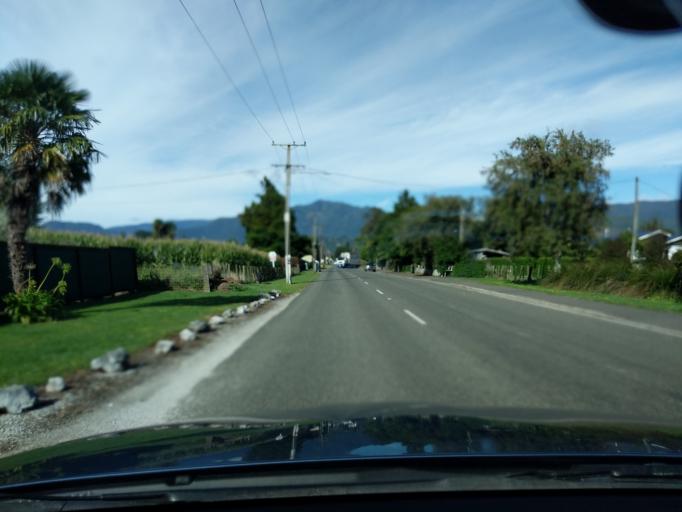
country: NZ
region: Tasman
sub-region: Tasman District
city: Takaka
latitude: -40.8574
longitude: 172.8112
